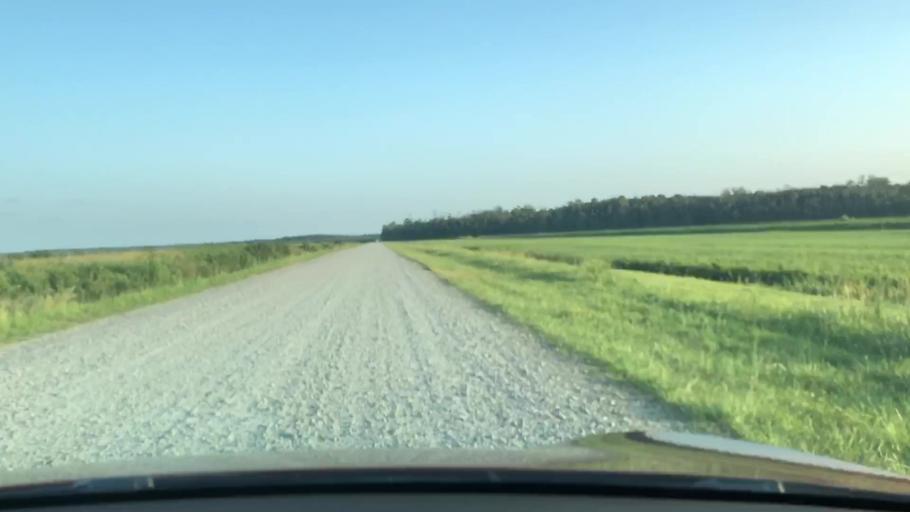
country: US
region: North Carolina
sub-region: Dare County
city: Manteo
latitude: 35.8506
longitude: -75.8616
